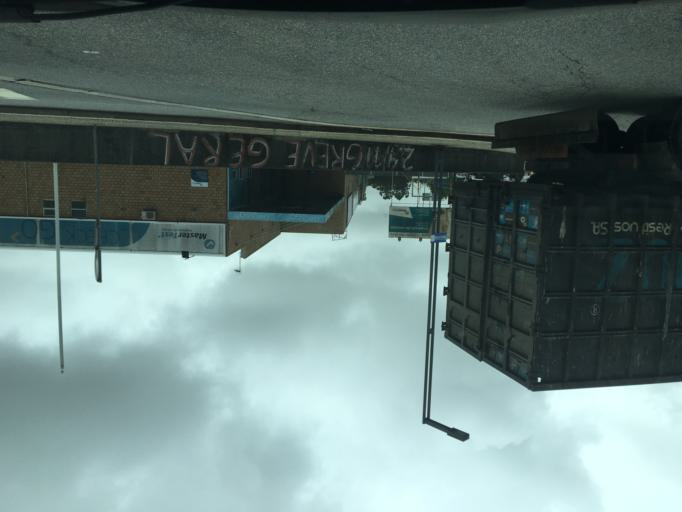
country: PT
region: Porto
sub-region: Maia
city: Maia
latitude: 41.2448
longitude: -8.6290
